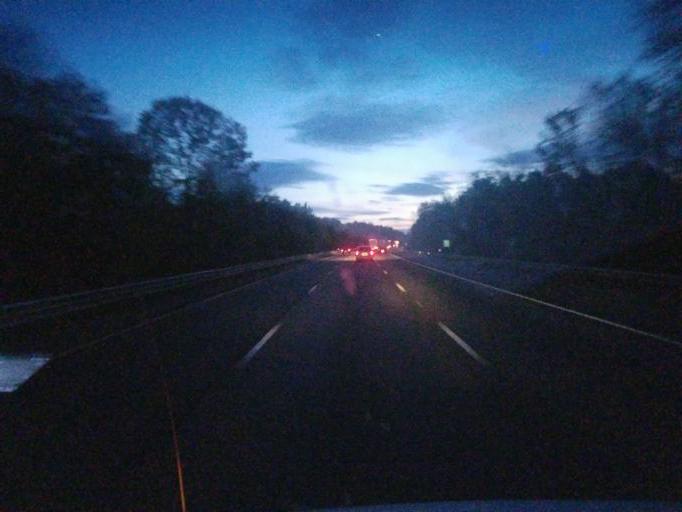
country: US
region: Massachusetts
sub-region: Worcester County
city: Bolton
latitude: 42.4134
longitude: -71.6065
